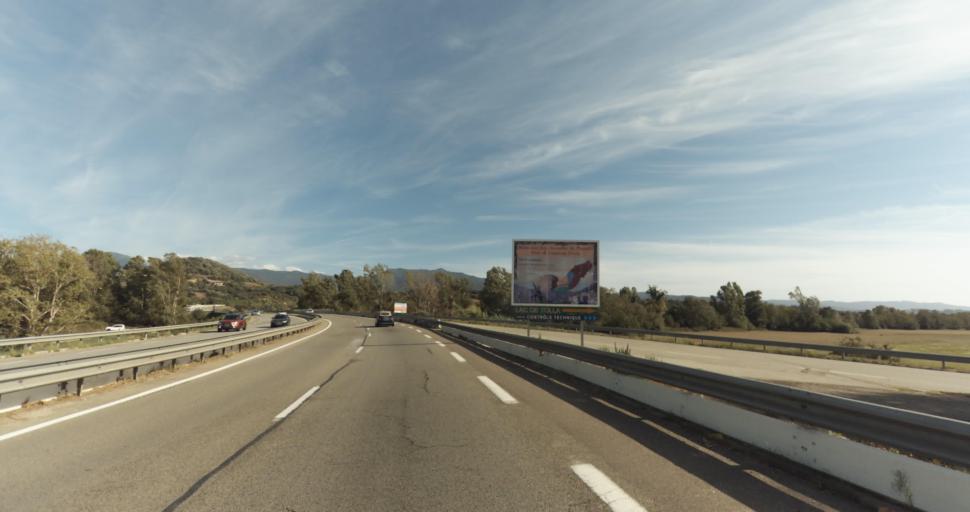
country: FR
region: Corsica
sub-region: Departement de la Corse-du-Sud
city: Afa
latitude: 41.9247
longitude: 8.8098
